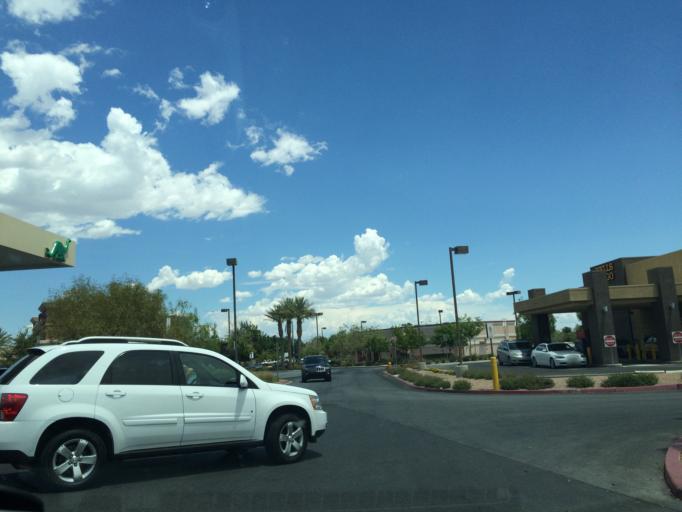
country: US
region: Nevada
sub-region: Clark County
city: North Las Vegas
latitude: 36.2875
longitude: -115.1795
